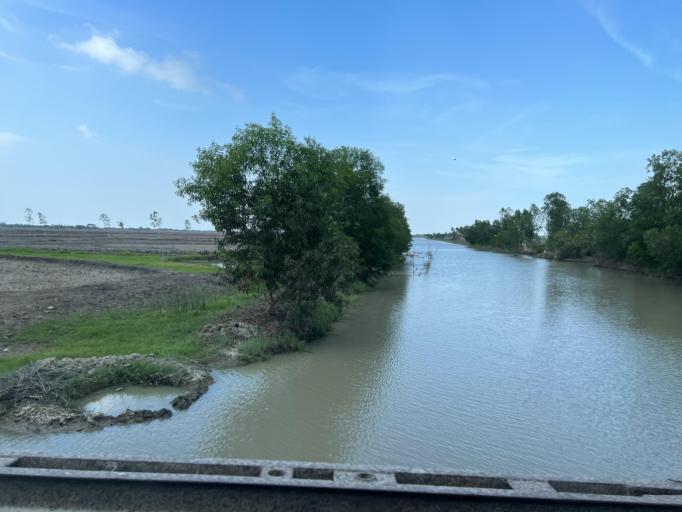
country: MM
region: Ayeyarwady
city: Pyapon
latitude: 16.0507
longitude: 95.6142
